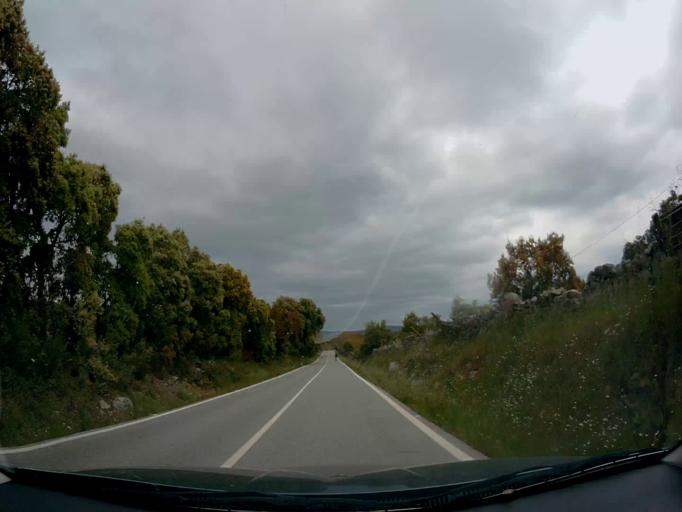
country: ES
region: Madrid
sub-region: Provincia de Madrid
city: Navalagamella
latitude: 40.4544
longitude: -4.1147
